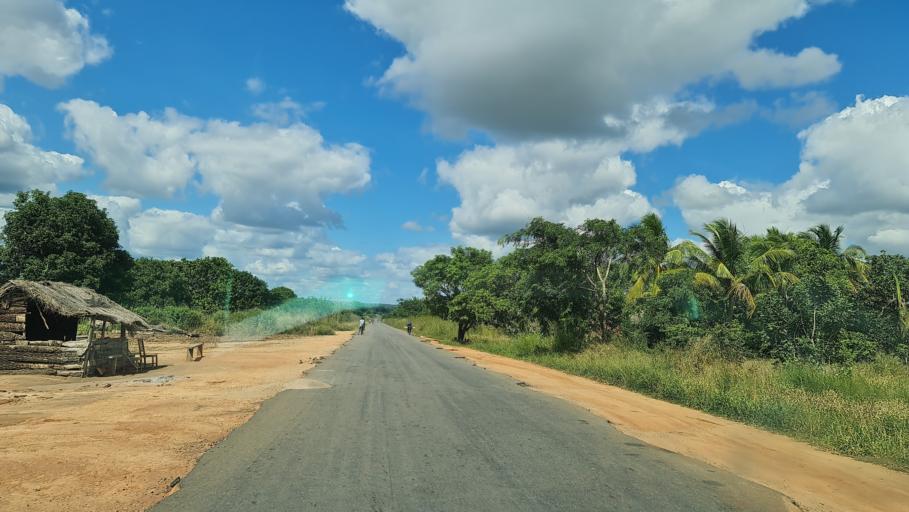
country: MZ
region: Zambezia
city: Quelimane
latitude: -17.5087
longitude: 36.2512
